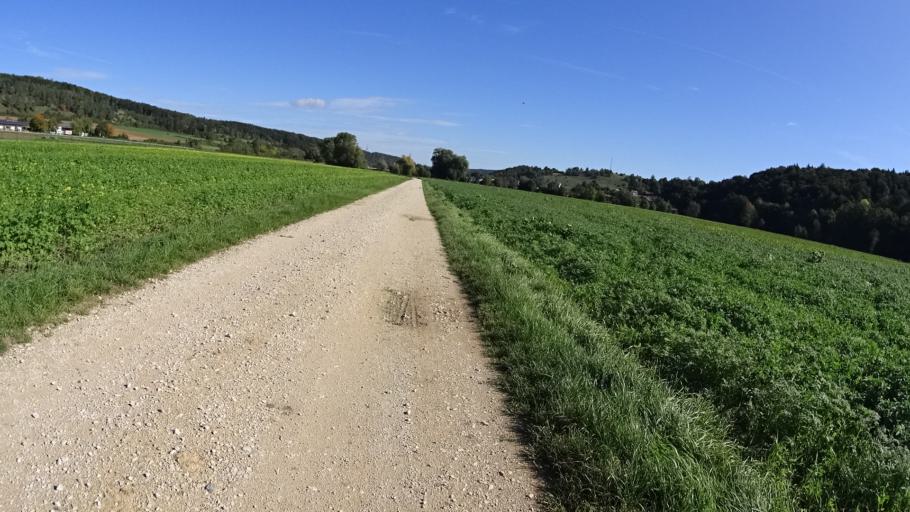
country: DE
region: Bavaria
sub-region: Upper Bavaria
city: Eichstaett
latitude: 48.8834
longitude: 11.2518
